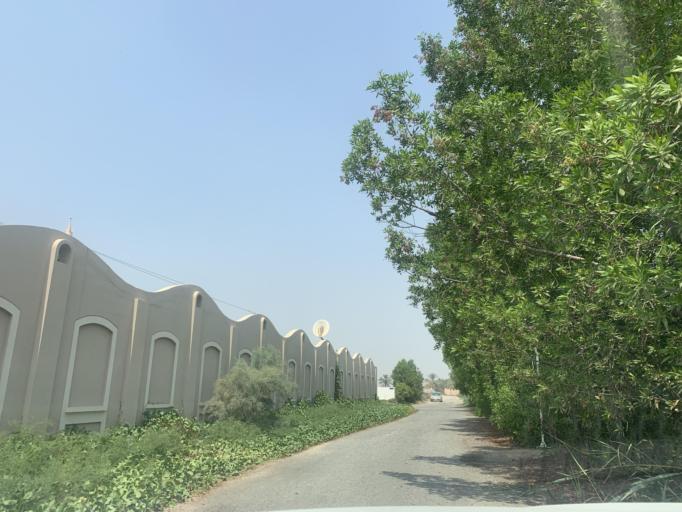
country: BH
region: Central Governorate
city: Madinat Hamad
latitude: 26.1610
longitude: 50.4540
